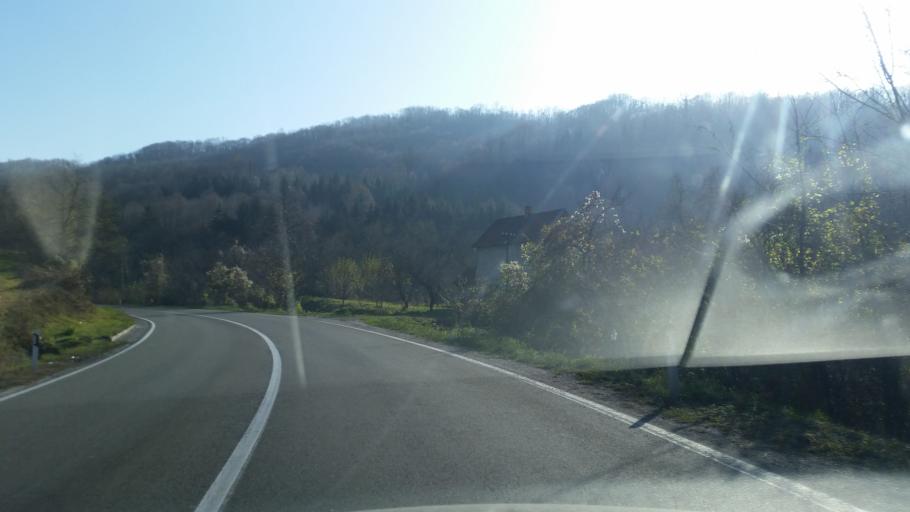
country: RS
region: Central Serbia
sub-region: Kolubarski Okrug
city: Ljig
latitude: 44.2003
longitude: 20.2348
